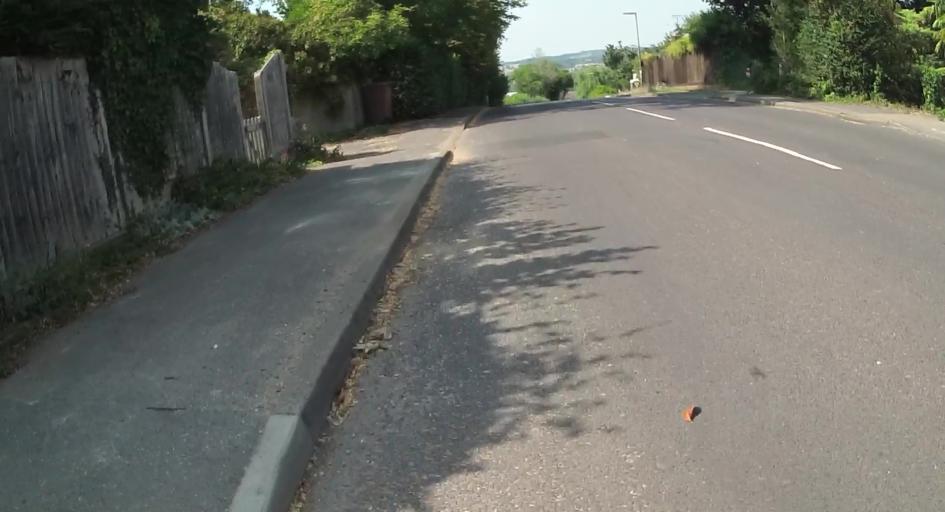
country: GB
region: England
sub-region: Surrey
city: Farnham
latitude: 51.1997
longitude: -0.8060
